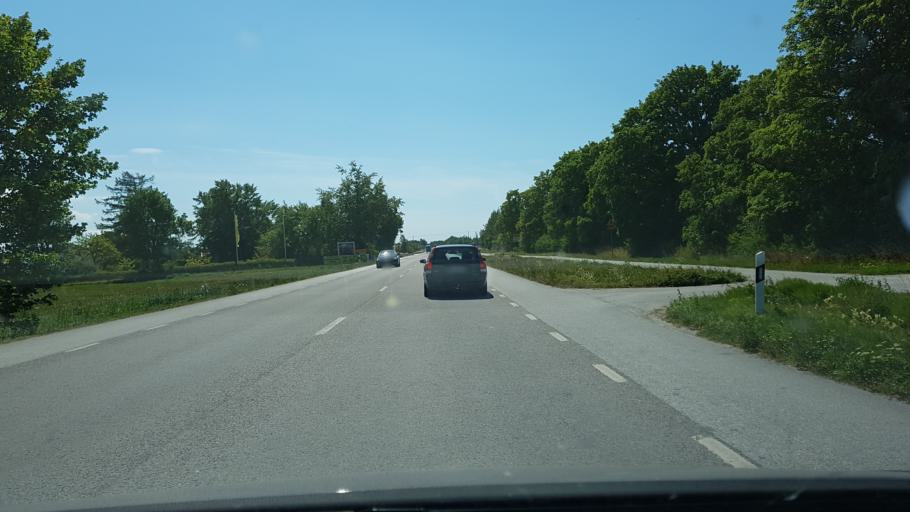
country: SE
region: Gotland
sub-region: Gotland
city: Vibble
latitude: 57.5273
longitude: 18.1743
